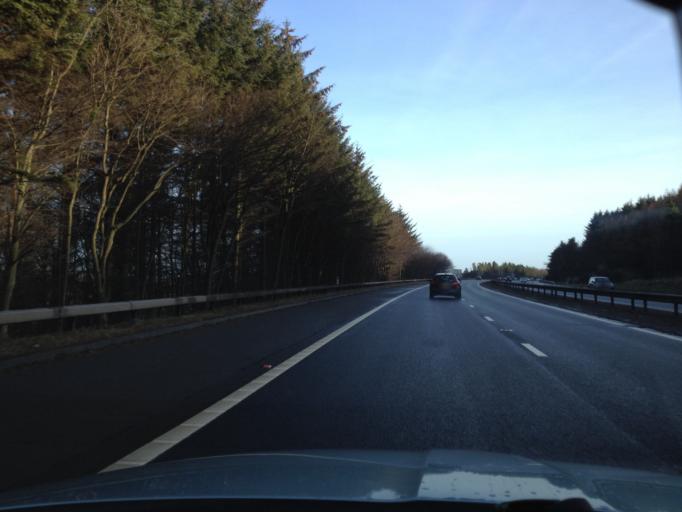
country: GB
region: Scotland
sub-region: West Lothian
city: Livingston
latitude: 55.9152
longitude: -3.5519
